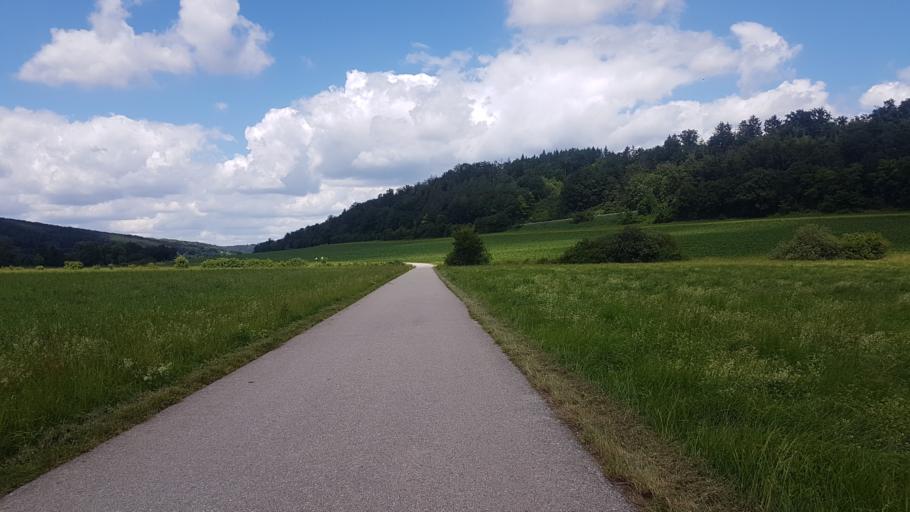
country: DE
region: Bavaria
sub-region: Upper Bavaria
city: Eichstaett
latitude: 48.8780
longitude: 11.1625
